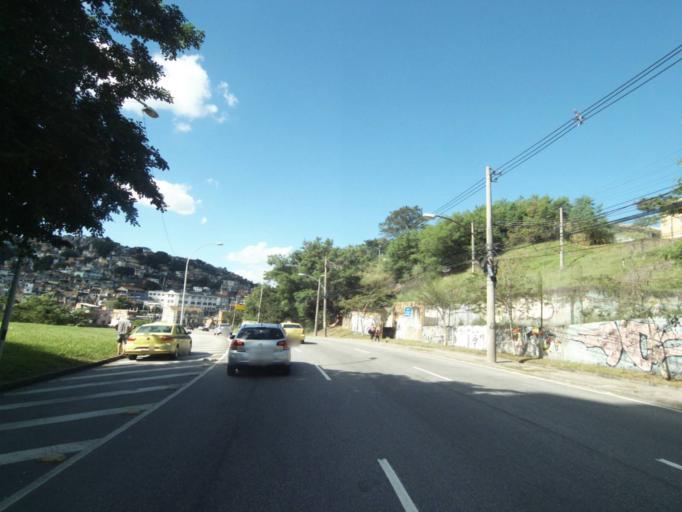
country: BR
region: Rio de Janeiro
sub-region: Rio De Janeiro
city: Rio de Janeiro
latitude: -22.9063
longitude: -43.2424
